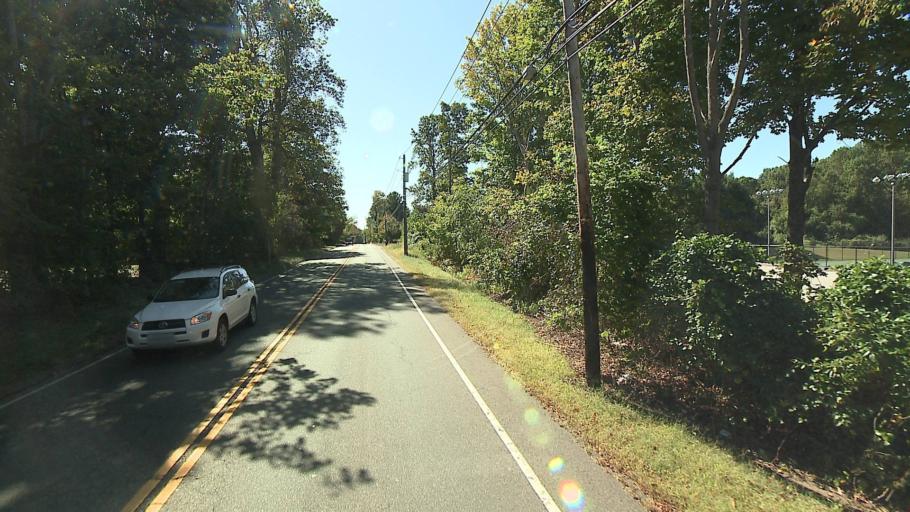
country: US
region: Connecticut
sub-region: New Haven County
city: City of Milford (balance)
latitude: 41.2499
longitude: -73.0525
